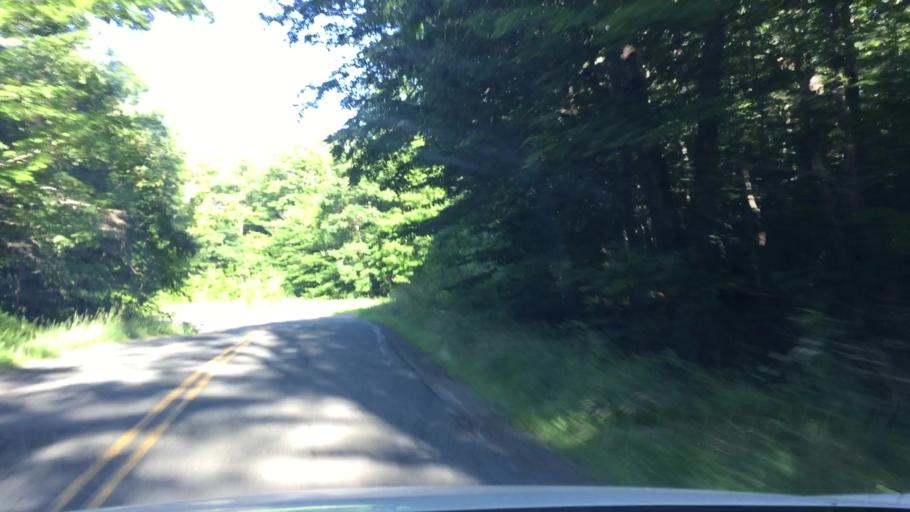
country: US
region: Massachusetts
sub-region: Berkshire County
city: Becket
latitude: 42.3009
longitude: -73.1347
